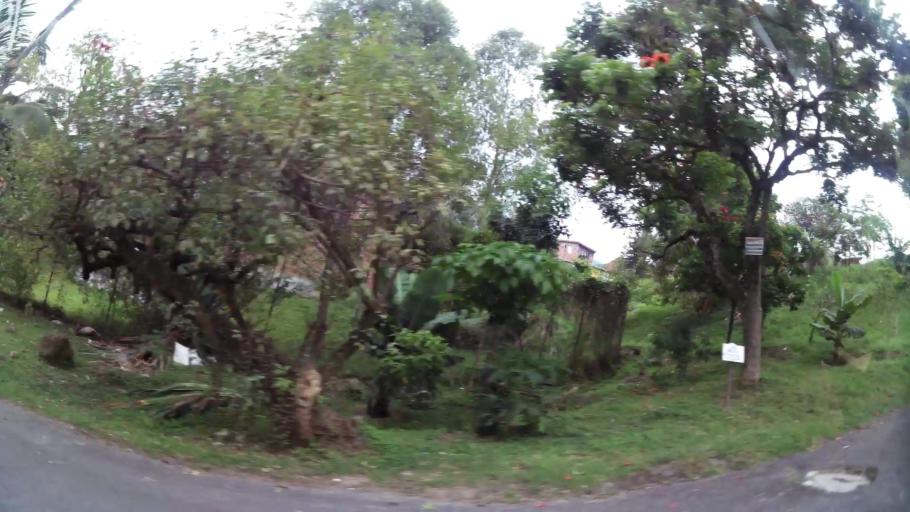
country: CO
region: Antioquia
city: Medellin
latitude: 6.2334
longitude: -75.5440
